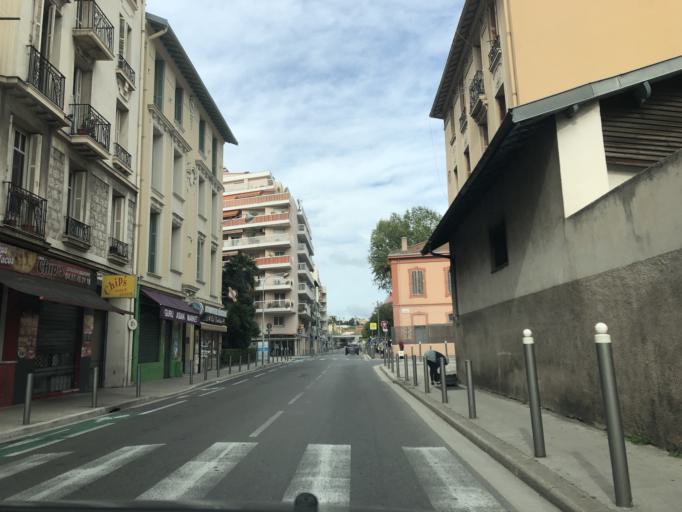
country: FR
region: Provence-Alpes-Cote d'Azur
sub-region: Departement des Alpes-Maritimes
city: Villefranche-sur-Mer
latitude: 43.7084
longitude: 7.2907
